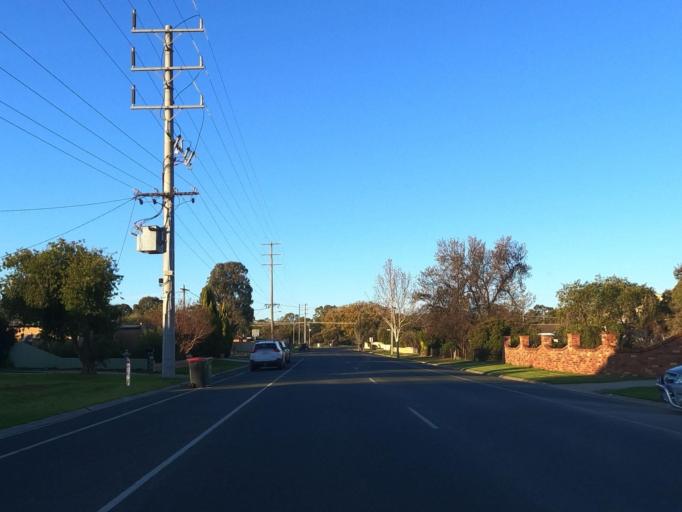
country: AU
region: Victoria
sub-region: Swan Hill
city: Swan Hill
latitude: -35.3594
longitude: 143.5598
